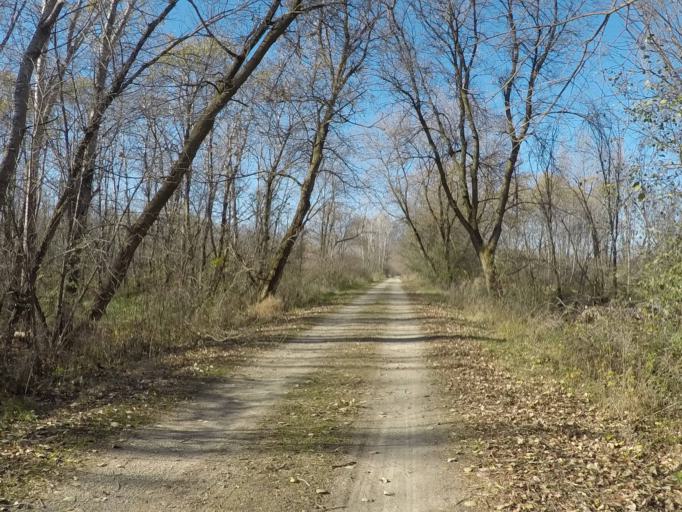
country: US
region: Wisconsin
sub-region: Dane County
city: Deerfield
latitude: 43.0427
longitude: -89.0356
